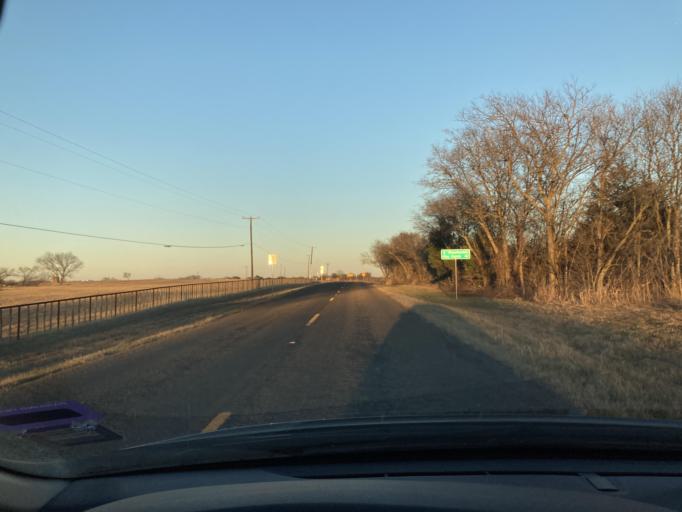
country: US
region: Texas
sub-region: Ellis County
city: Waxahachie
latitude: 32.3431
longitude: -96.8760
